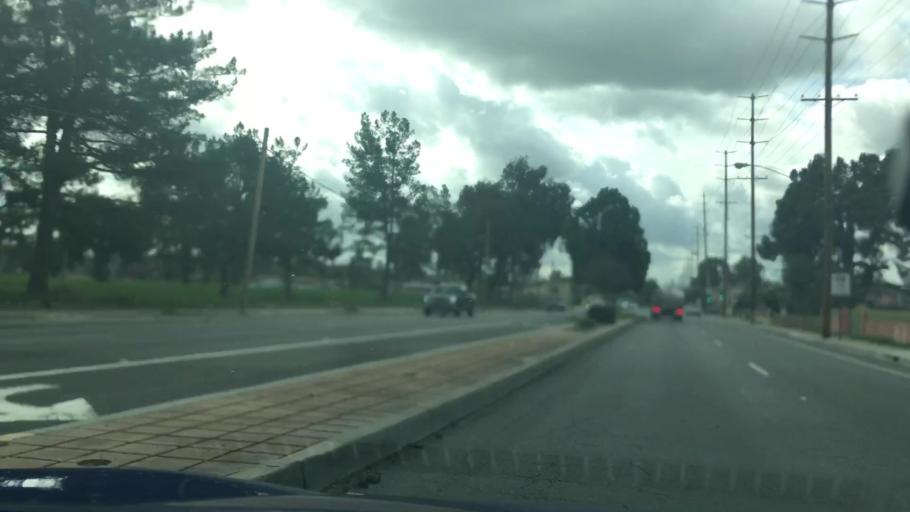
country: US
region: California
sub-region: Riverside County
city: Highgrove
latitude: 34.0083
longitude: -117.3636
